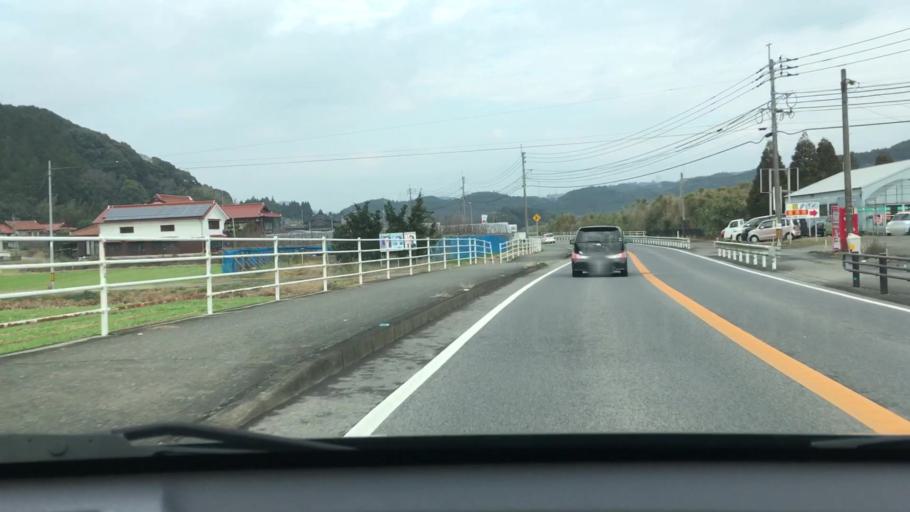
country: JP
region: Saga Prefecture
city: Imaricho-ko
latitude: 33.3255
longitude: 129.9292
